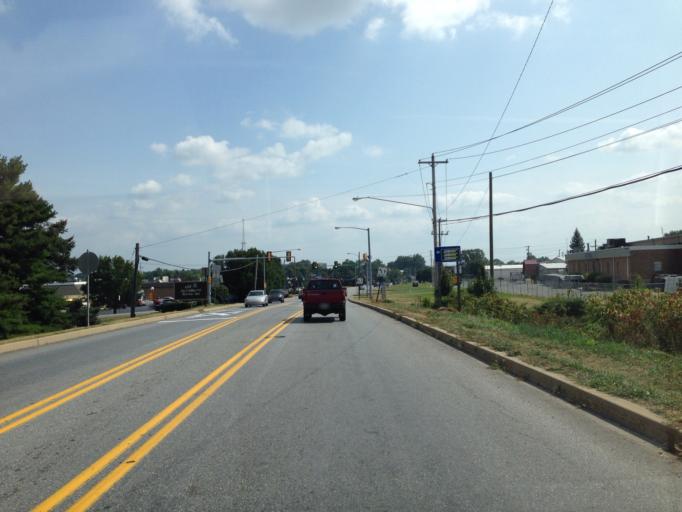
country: US
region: Pennsylvania
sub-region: Lancaster County
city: Mountville
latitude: 40.0493
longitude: -76.3941
